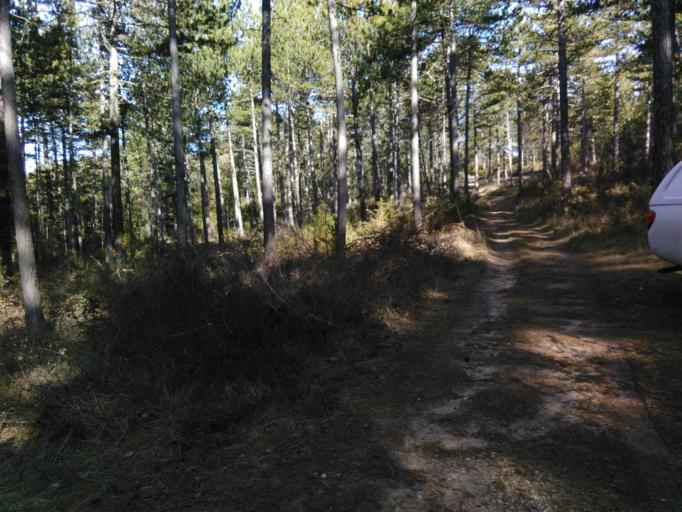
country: FR
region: Provence-Alpes-Cote d'Azur
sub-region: Departement du Vaucluse
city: Venasque
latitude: 43.9628
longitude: 5.1725
